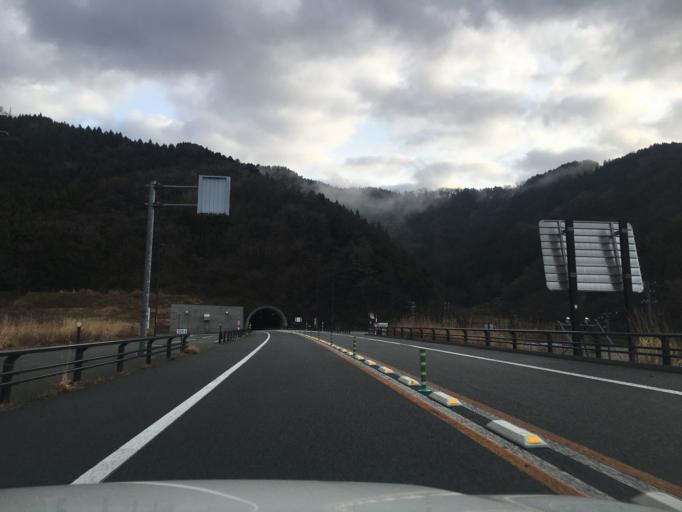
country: JP
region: Yamagata
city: Tsuruoka
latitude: 38.6057
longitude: 139.5868
